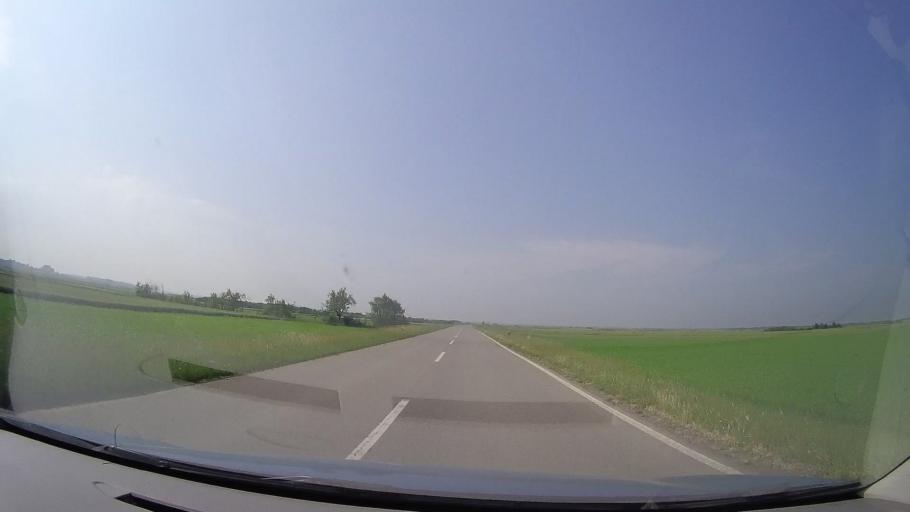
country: RS
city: Jasa Tomic
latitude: 45.4257
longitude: 20.8371
